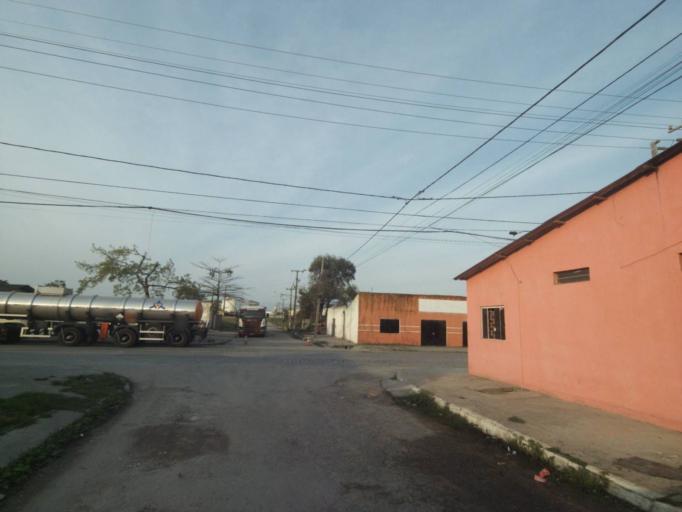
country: BR
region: Parana
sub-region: Paranagua
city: Paranagua
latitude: -25.5116
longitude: -48.5380
